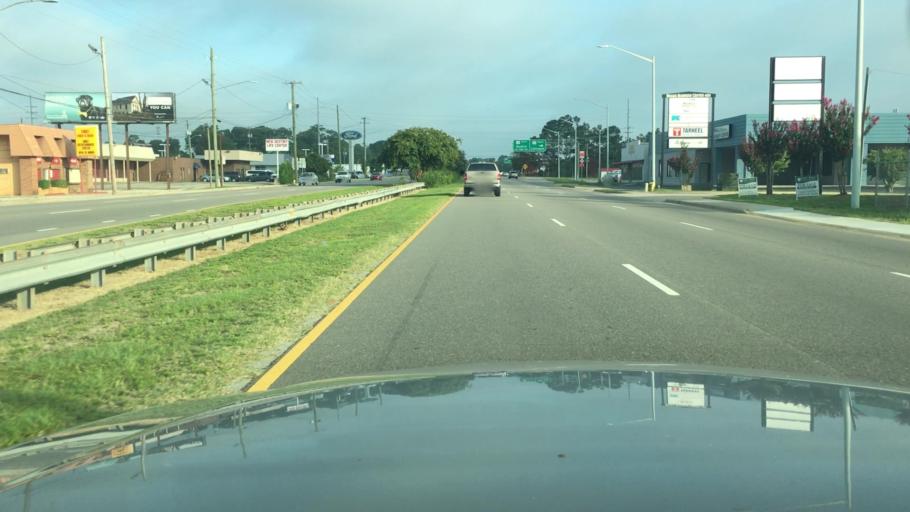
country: US
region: North Carolina
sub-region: Cumberland County
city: Fayetteville
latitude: 35.0845
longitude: -78.9480
